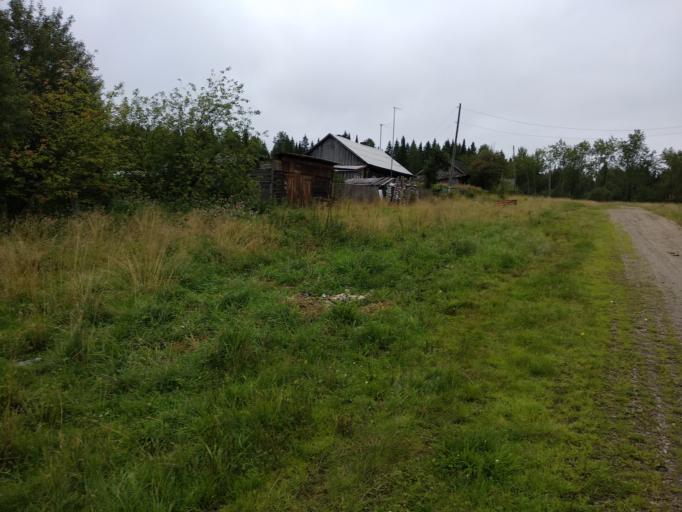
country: RU
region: Sverdlovsk
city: Serov
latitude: 59.8413
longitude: 60.7288
